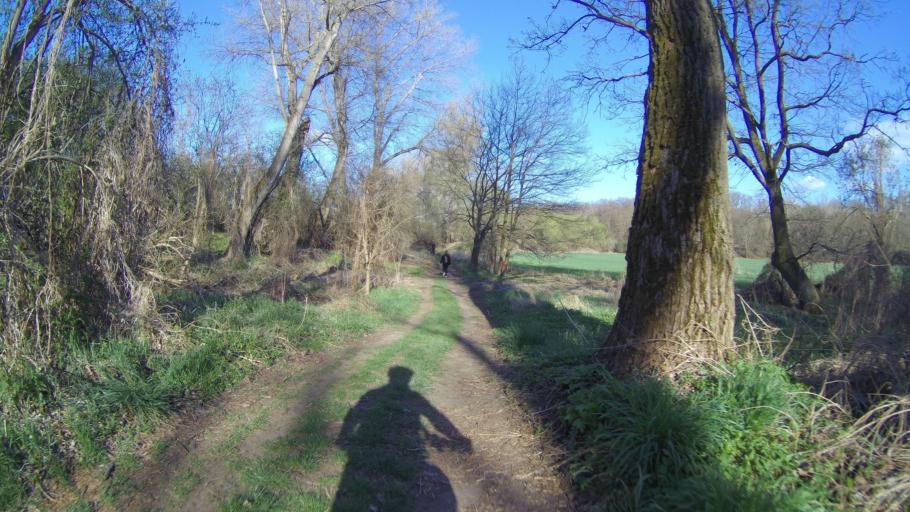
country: CZ
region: Ustecky
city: Zatec
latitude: 50.3367
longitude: 13.5741
